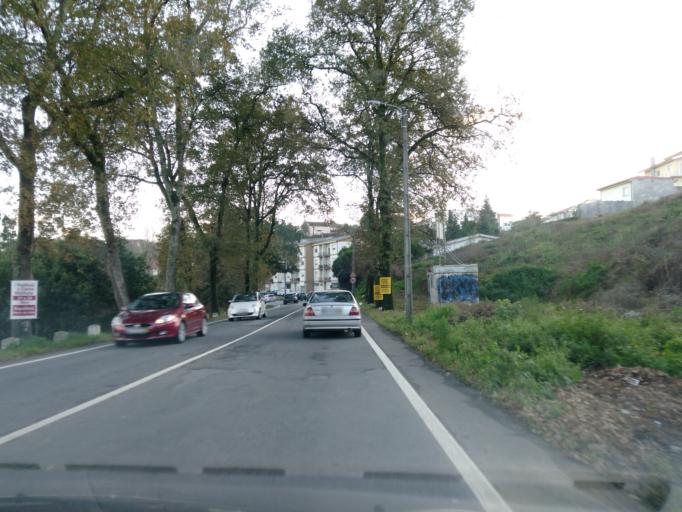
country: PT
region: Braga
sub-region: Braga
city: Braga
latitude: 41.5364
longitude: -8.4500
